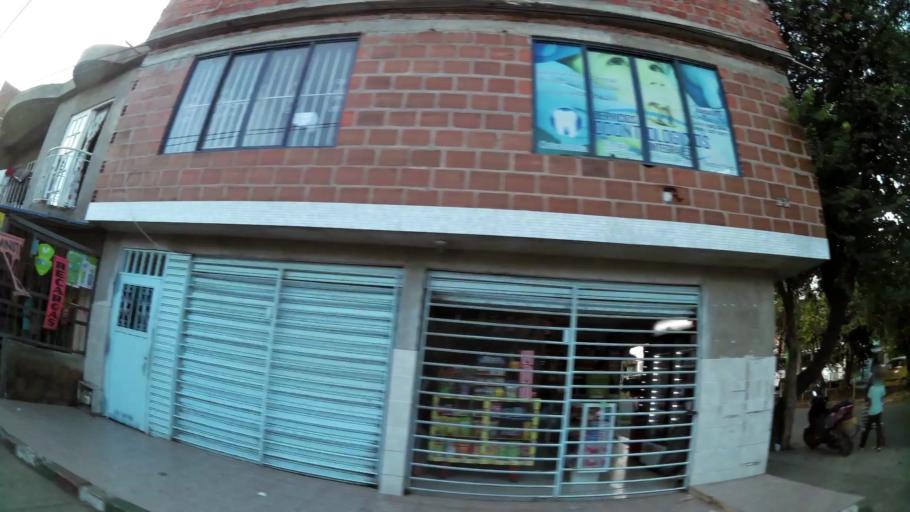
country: CO
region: Valle del Cauca
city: Cali
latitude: 3.4122
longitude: -76.5013
